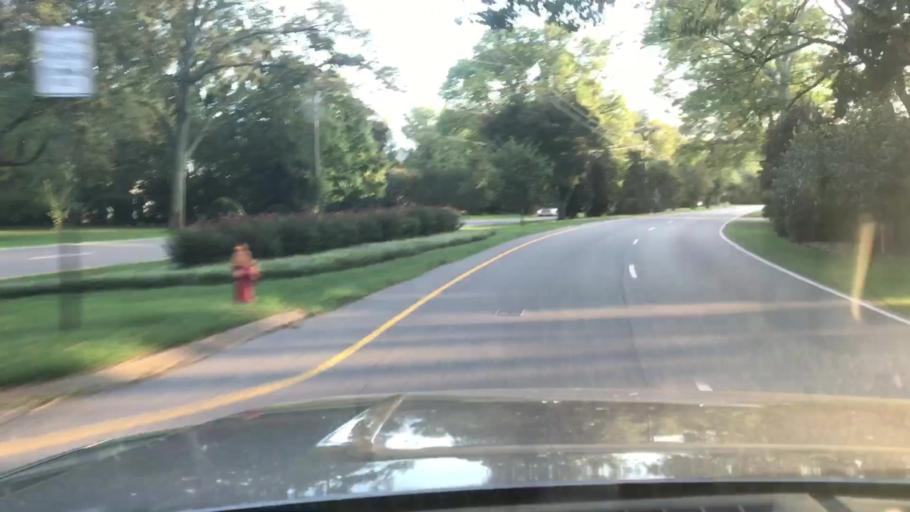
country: US
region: Tennessee
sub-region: Davidson County
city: Belle Meade
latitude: 36.0940
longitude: -86.8570
